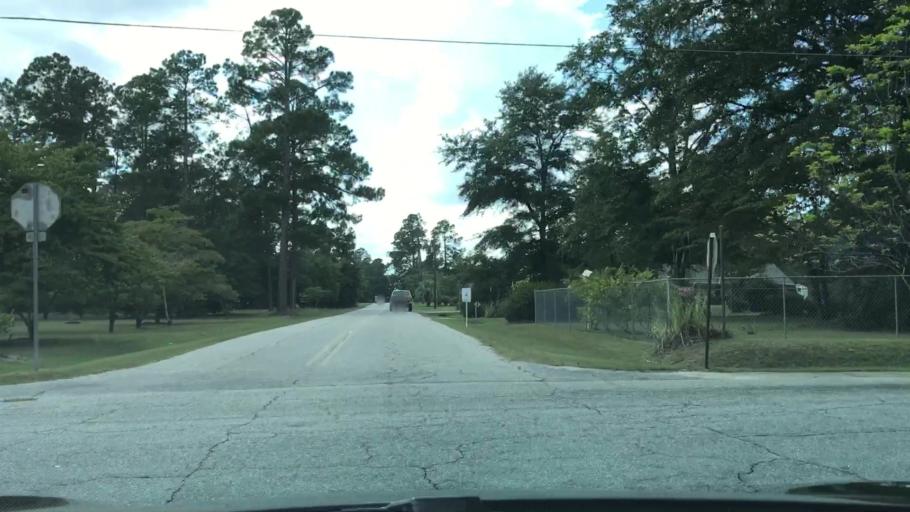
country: US
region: Georgia
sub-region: Jefferson County
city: Wadley
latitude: 32.8710
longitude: -82.3975
